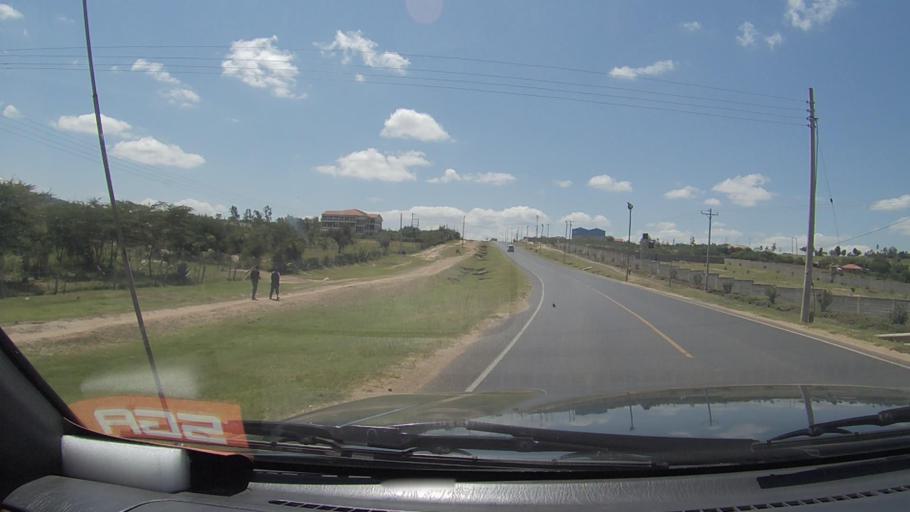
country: KE
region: Machakos
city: Machakos
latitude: -1.5341
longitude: 37.1933
